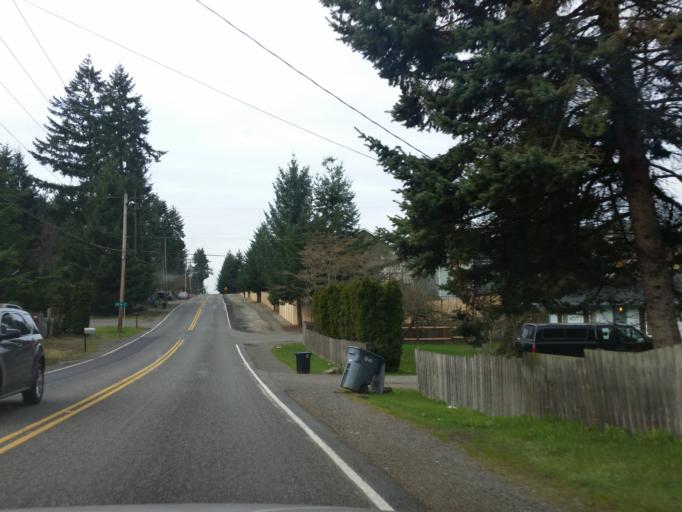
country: US
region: Washington
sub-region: Pierce County
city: South Hill
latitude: 47.1329
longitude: -122.2791
